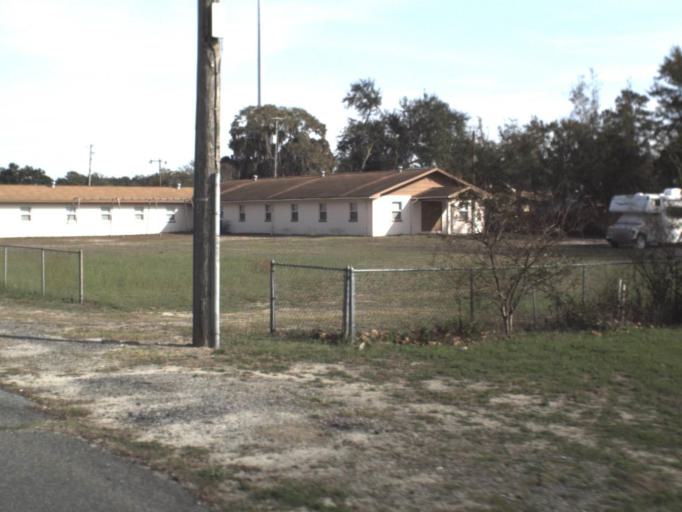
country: US
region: Florida
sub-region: Bay County
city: Parker
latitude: 30.1311
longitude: -85.6067
